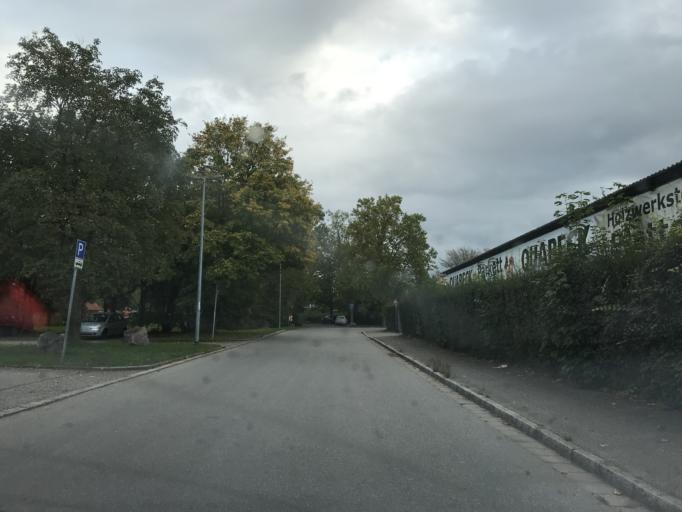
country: DE
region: Baden-Wuerttemberg
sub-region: Freiburg Region
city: Loerrach
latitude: 47.6257
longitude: 7.6608
